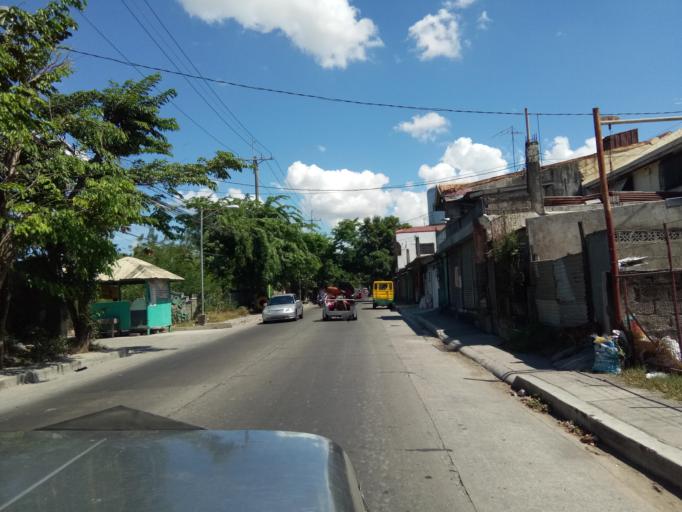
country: PH
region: Calabarzon
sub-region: Province of Cavite
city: Dasmarinas
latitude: 14.3486
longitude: 120.9451
